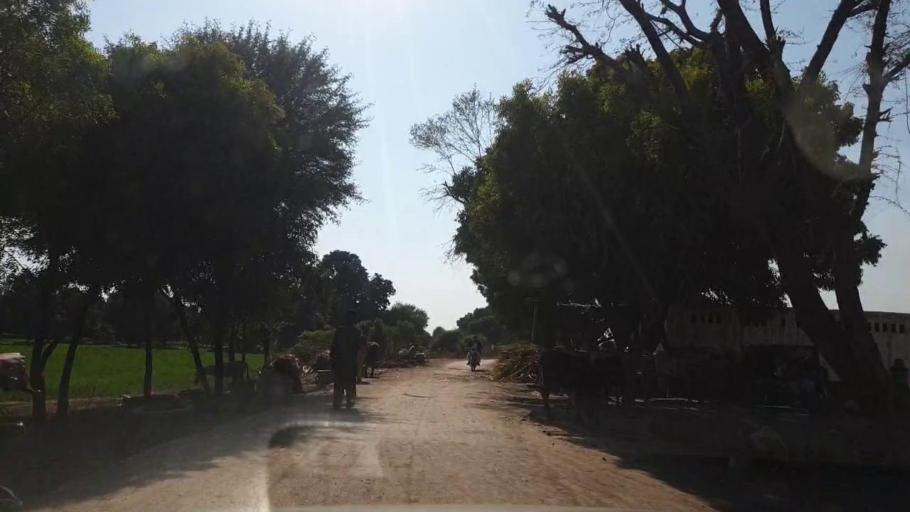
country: PK
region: Sindh
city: Tando Allahyar
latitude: 25.4763
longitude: 68.6952
